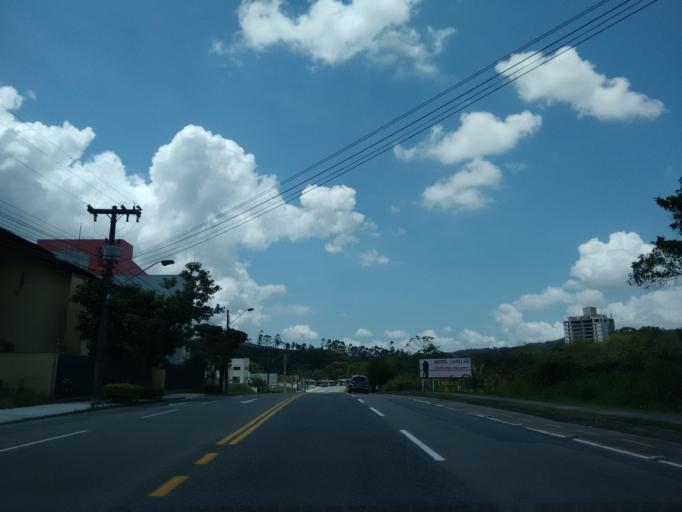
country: BR
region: Santa Catarina
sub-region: Blumenau
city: Blumenau
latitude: -26.9019
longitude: -49.0393
